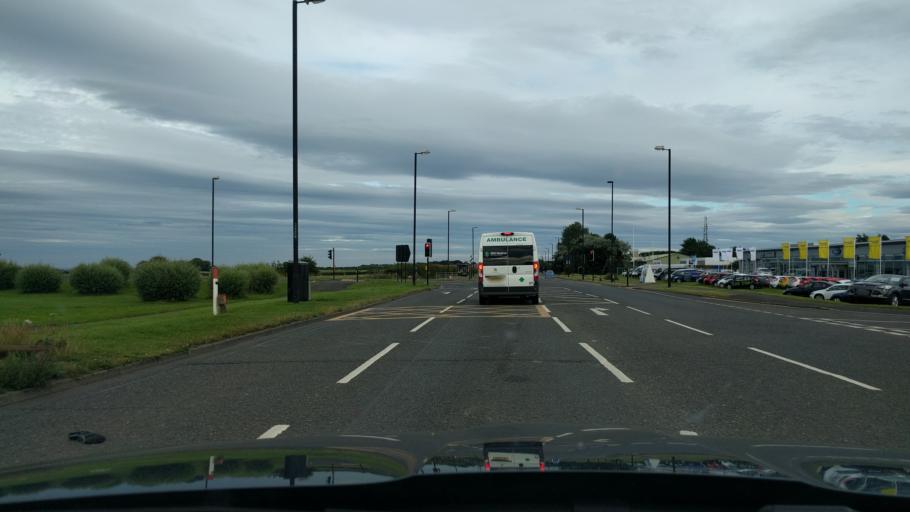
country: GB
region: England
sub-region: Borough of North Tyneside
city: Shiremoor
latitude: 55.0276
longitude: -1.5060
